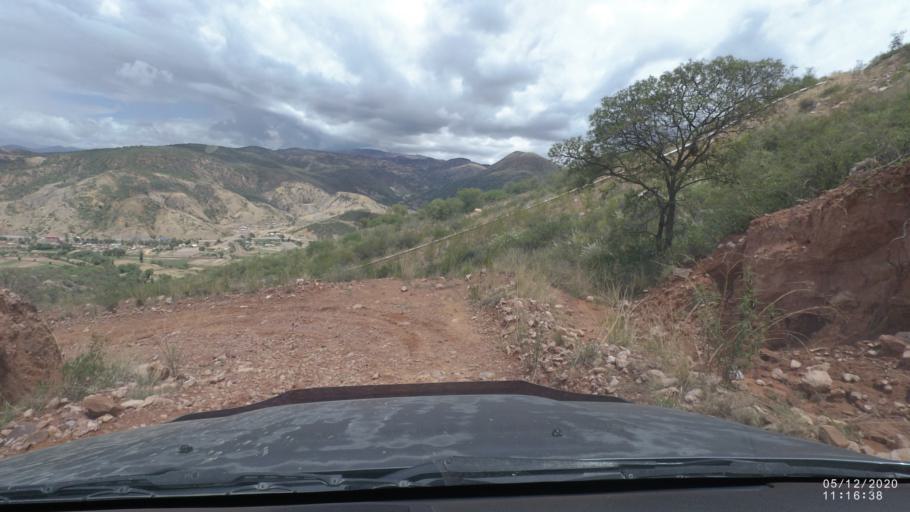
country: BO
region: Cochabamba
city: Sipe Sipe
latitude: -17.5513
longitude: -66.3302
